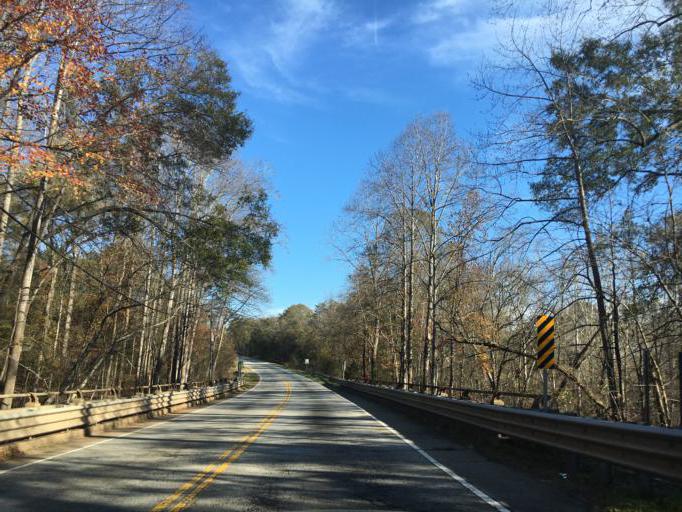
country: US
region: South Carolina
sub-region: Spartanburg County
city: Wellford
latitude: 34.9597
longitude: -82.0772
